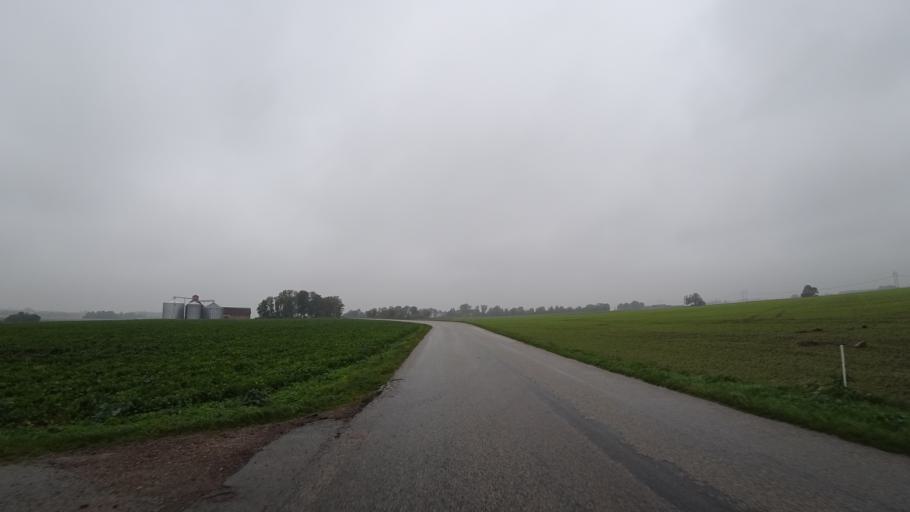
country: SE
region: Skane
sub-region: Kavlinge Kommun
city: Kaevlinge
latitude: 55.7997
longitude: 13.1629
